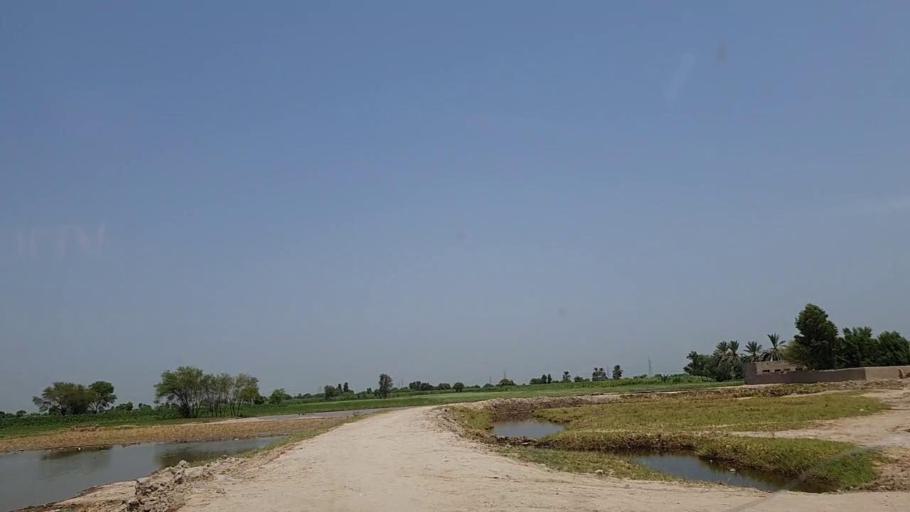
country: PK
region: Sindh
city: Ghotki
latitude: 27.9939
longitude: 69.3627
